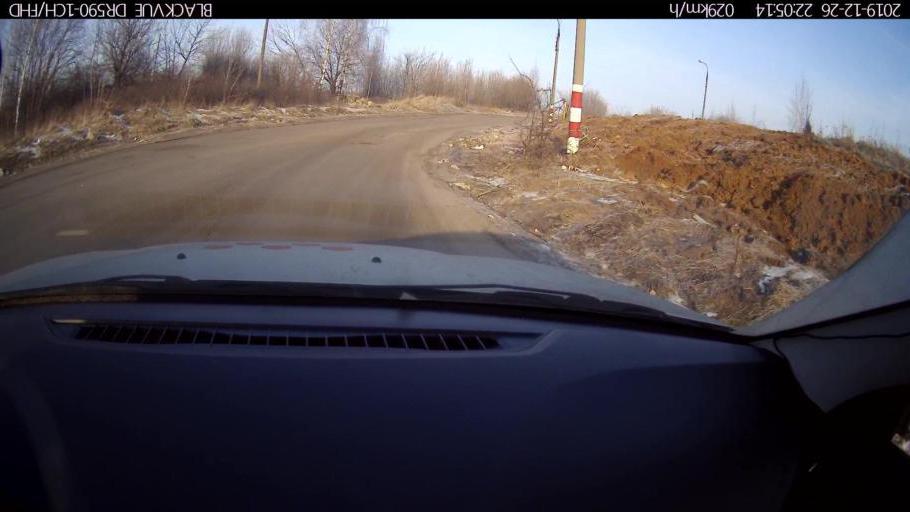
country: RU
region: Nizjnij Novgorod
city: Afonino
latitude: 56.1955
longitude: 44.0896
